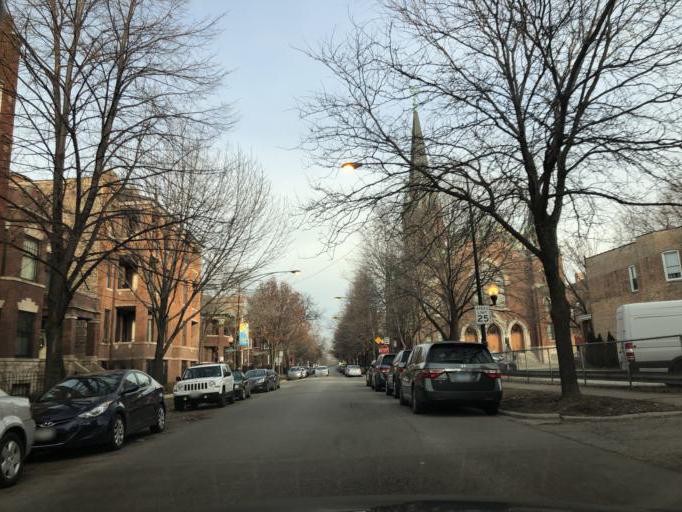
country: US
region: Illinois
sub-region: Cook County
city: Chicago
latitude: 41.8998
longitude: -87.6845
